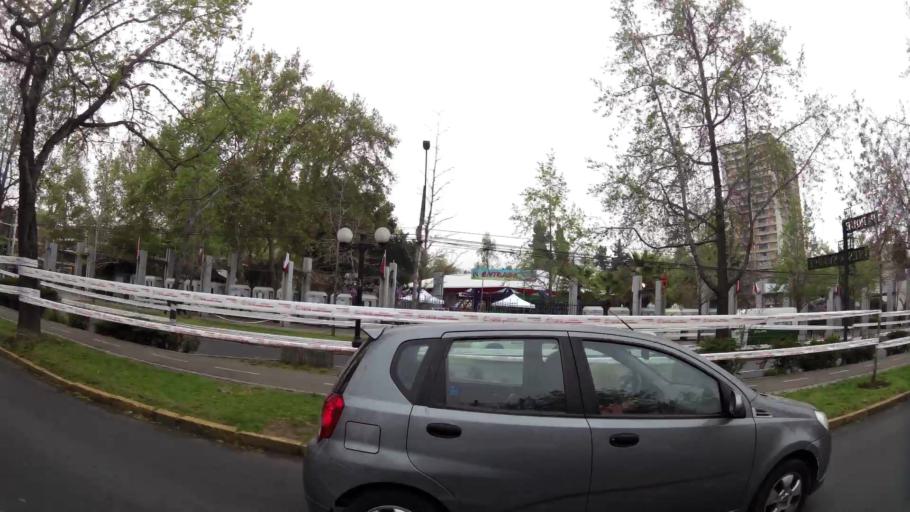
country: CL
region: Santiago Metropolitan
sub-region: Provincia de Santiago
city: Villa Presidente Frei, Nunoa, Santiago, Chile
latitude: -33.4386
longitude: -70.6118
